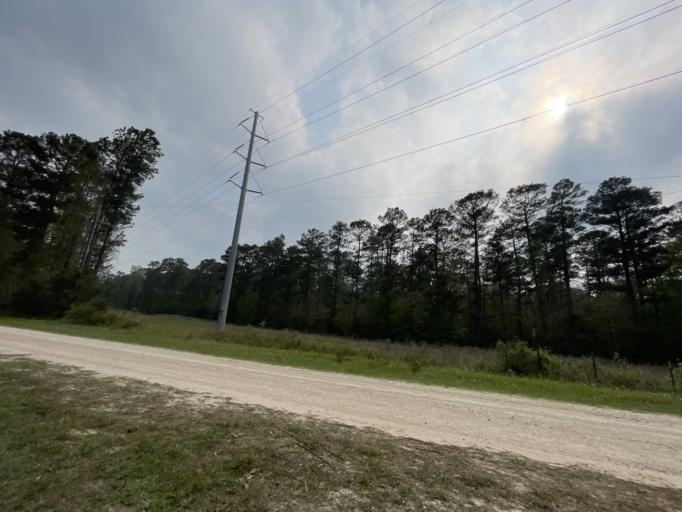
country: US
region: Texas
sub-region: Walker County
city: Huntsville
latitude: 30.6512
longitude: -95.4845
